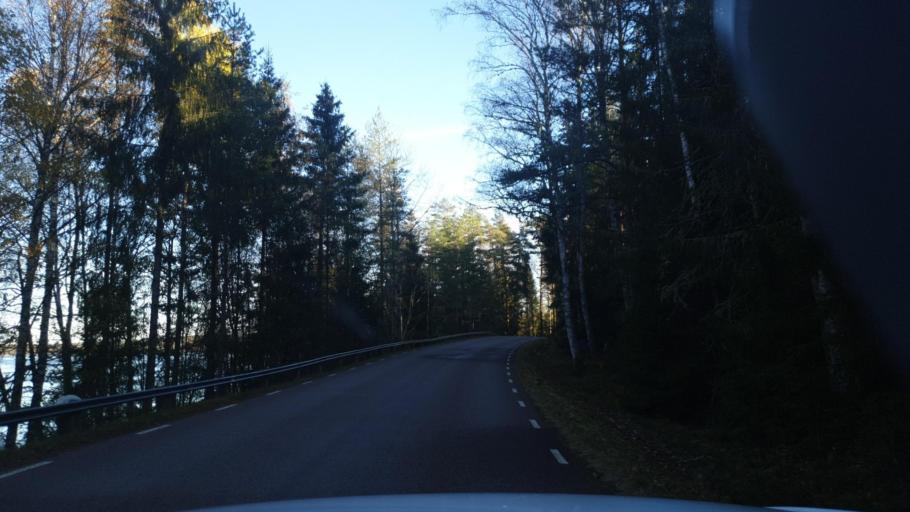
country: SE
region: Vaermland
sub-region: Grums Kommun
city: Grums
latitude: 59.4108
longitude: 13.0739
